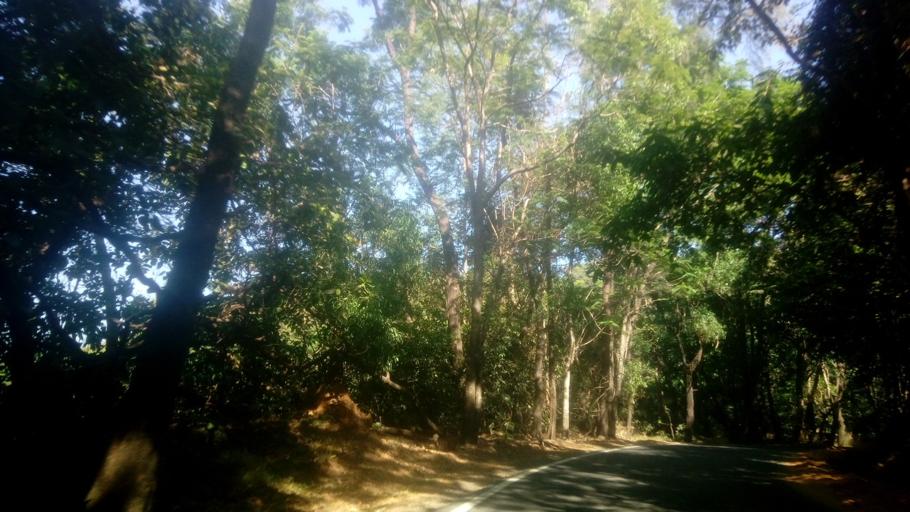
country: IN
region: Goa
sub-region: North Goa
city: Valpoy
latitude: 15.6128
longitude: 74.1180
